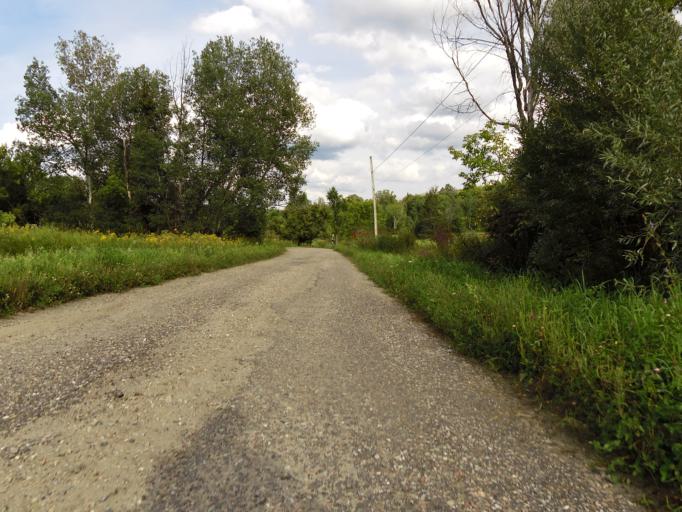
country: CA
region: Quebec
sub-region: Outaouais
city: Wakefield
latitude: 45.6432
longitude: -76.0068
